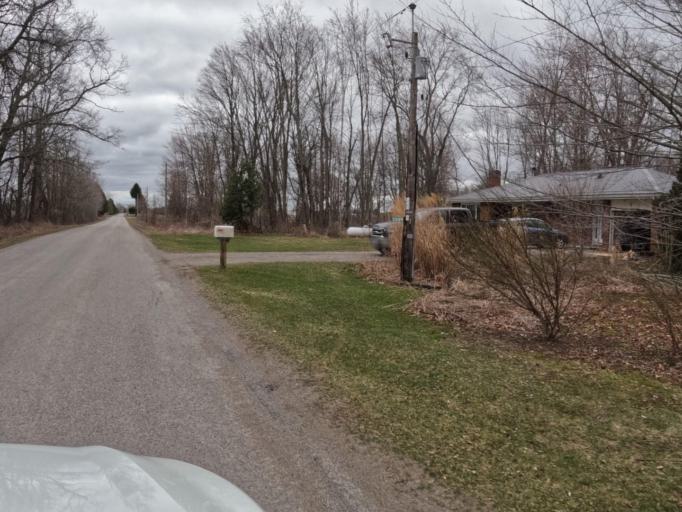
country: CA
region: Ontario
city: Norfolk County
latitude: 42.9759
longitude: -80.4022
